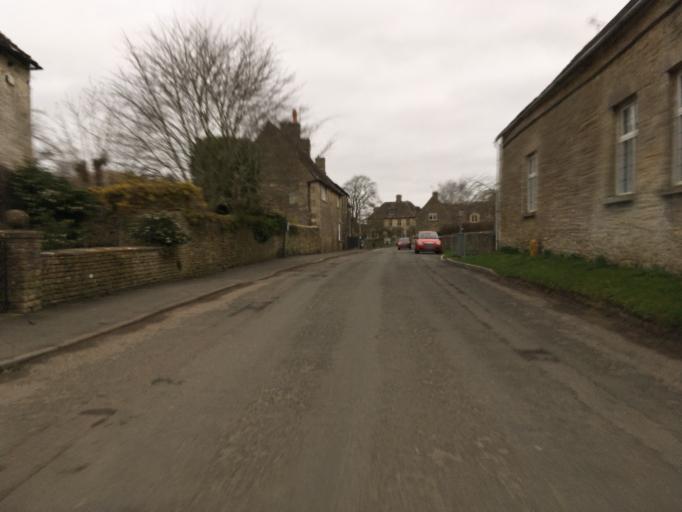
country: GB
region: England
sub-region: Wiltshire
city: Cricklade
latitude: 51.7062
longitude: -1.8572
